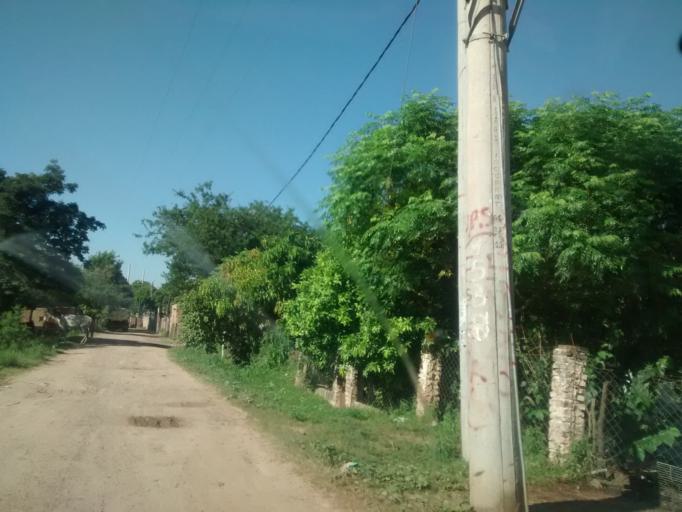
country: AR
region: Chaco
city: Resistencia
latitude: -27.4265
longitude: -58.9835
